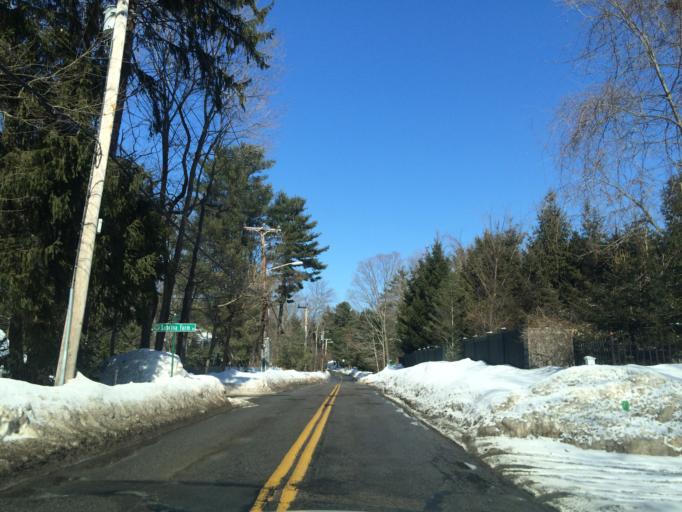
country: US
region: Massachusetts
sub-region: Norfolk County
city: Wellesley
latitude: 42.2789
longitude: -71.2878
